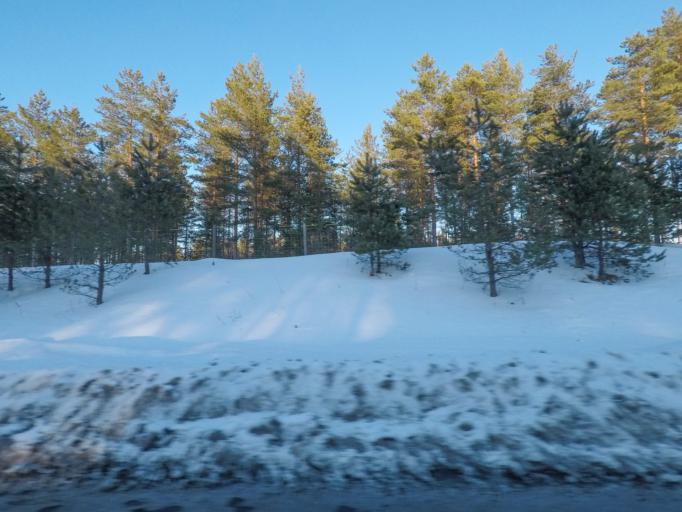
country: FI
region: Southern Savonia
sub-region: Mikkeli
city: Pertunmaa
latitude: 61.4183
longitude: 26.4350
